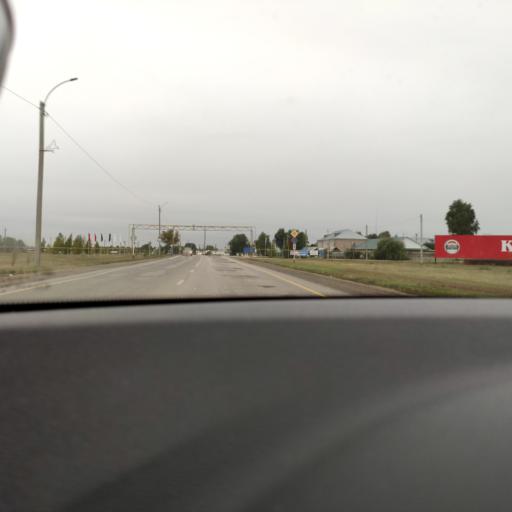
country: RU
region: Samara
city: Krasnyy Yar
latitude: 53.4776
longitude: 50.3917
